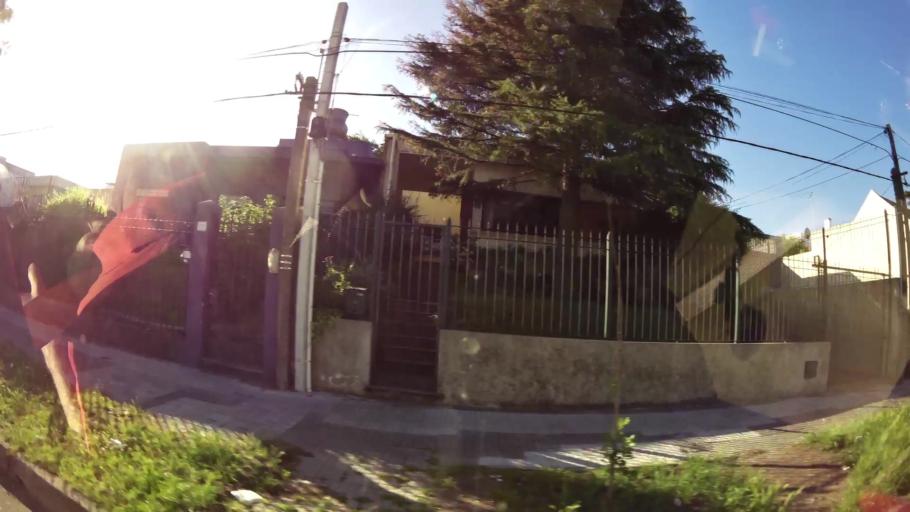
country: UY
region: Montevideo
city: Montevideo
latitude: -34.8449
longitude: -56.2031
